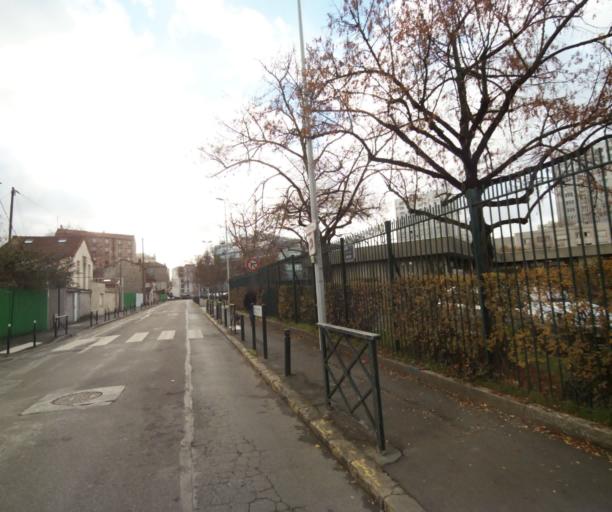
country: FR
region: Ile-de-France
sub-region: Departement des Hauts-de-Seine
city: Puteaux
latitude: 48.8865
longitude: 2.2260
